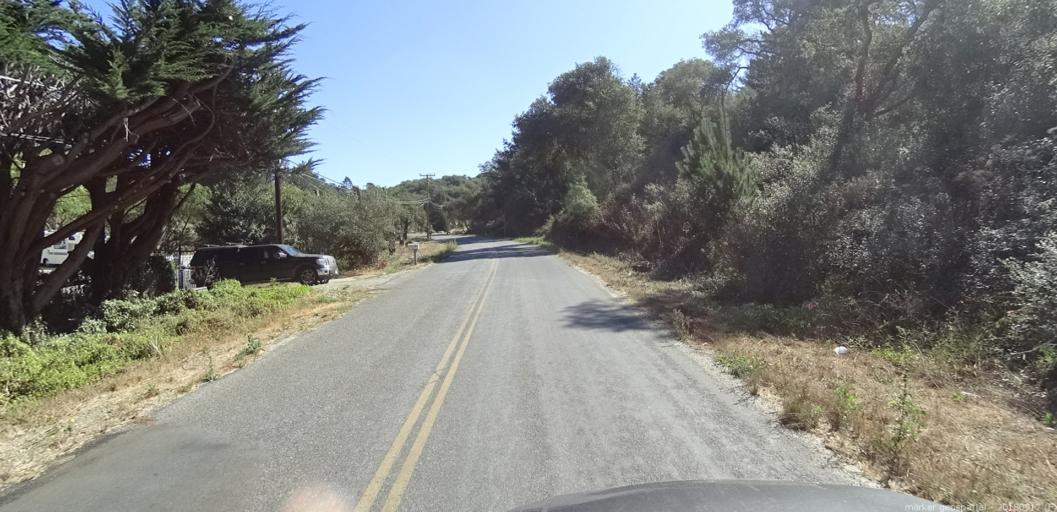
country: US
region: California
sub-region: Monterey County
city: Elkhorn
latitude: 36.8364
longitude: -121.7040
